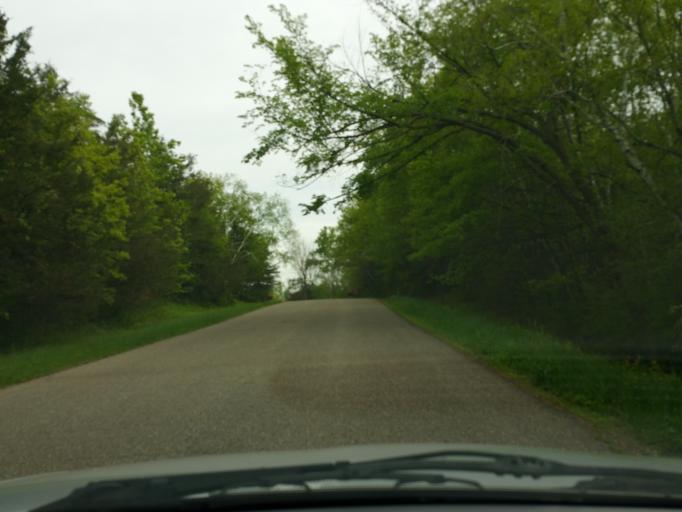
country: US
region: Wisconsin
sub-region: Saint Croix County
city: Hudson
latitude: 44.9444
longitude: -92.6836
